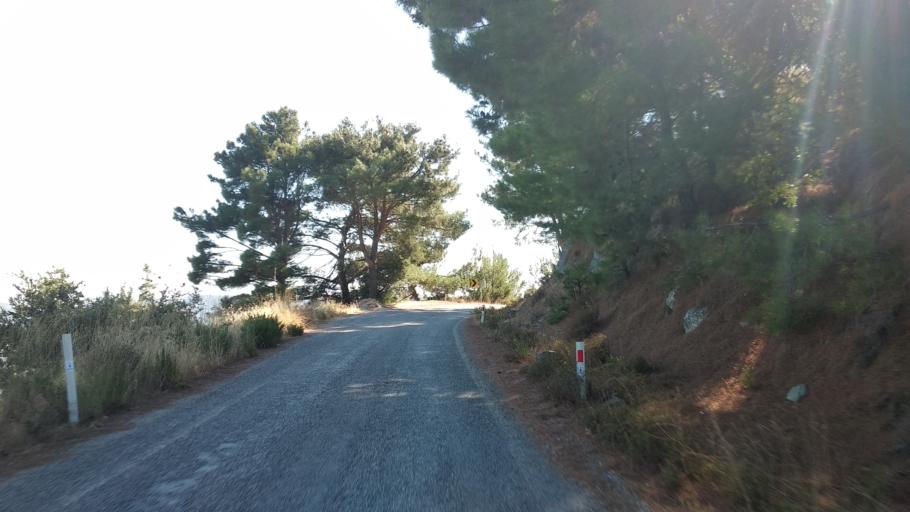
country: TR
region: Izmir
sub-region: Seferihisar
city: Seferhisar
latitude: 38.3230
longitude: 26.9378
